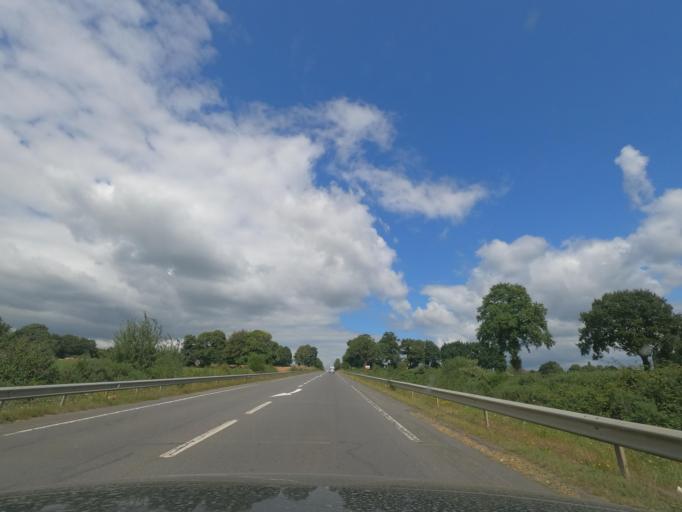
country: FR
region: Brittany
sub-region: Departement d'Ille-et-Vilaine
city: Lecousse
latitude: 48.3569
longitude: -1.2298
